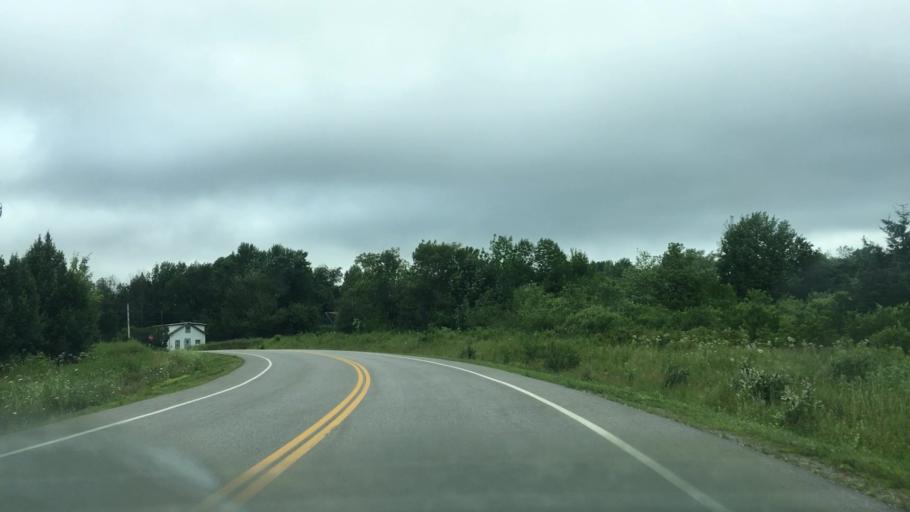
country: US
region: Maine
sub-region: Penobscot County
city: Veazie
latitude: 44.8428
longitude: -68.7438
